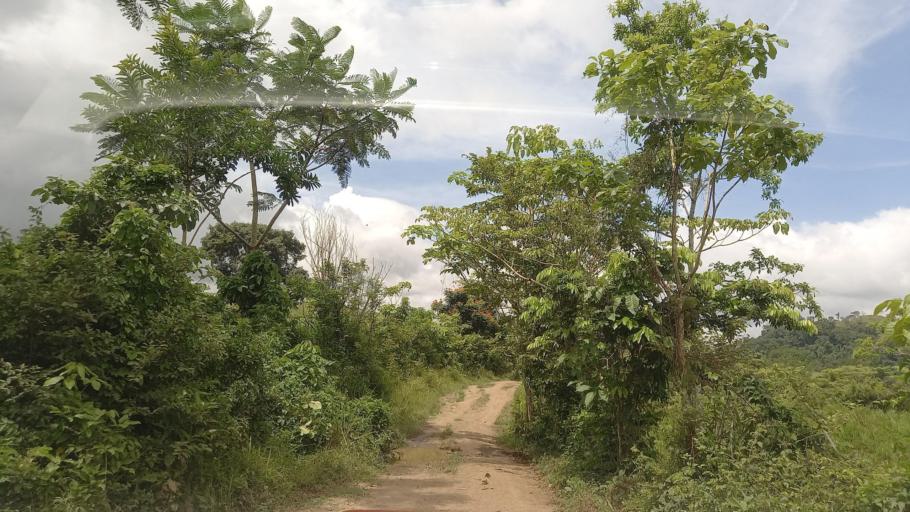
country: NI
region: Jinotega
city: San Jose de Bocay
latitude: 13.4167
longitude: -85.7047
